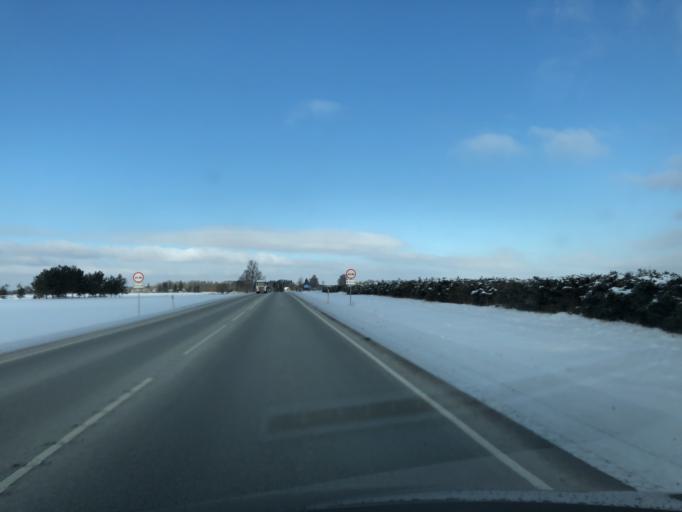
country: EE
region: Jaervamaa
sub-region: Paide linn
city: Paide
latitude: 58.7827
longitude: 25.7593
